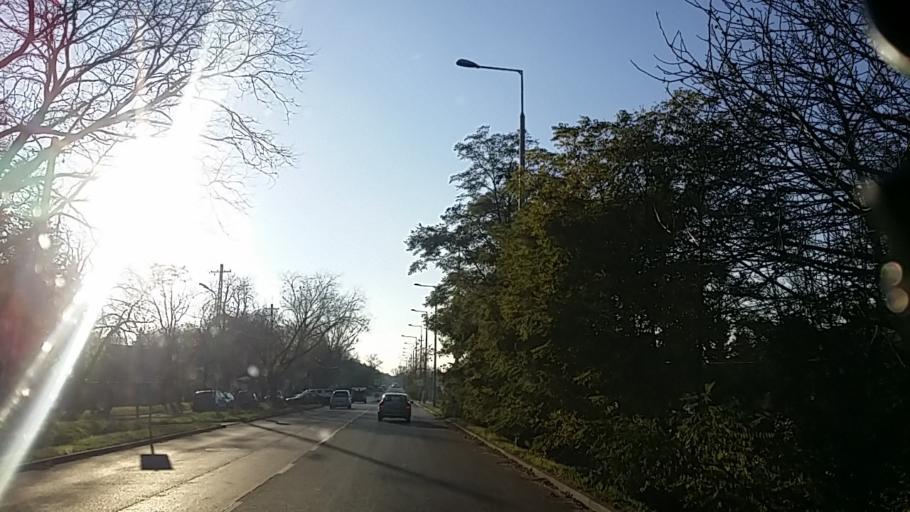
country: HU
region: Budapest
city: Budapest XVI. keruelet
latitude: 47.5142
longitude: 19.2022
